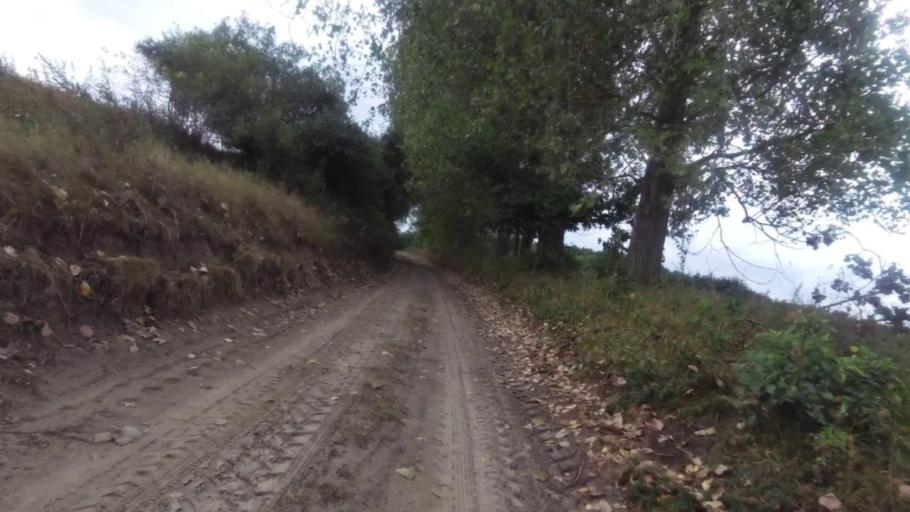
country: PL
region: West Pomeranian Voivodeship
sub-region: Powiat mysliborski
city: Boleszkowice
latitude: 52.6735
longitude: 14.6168
